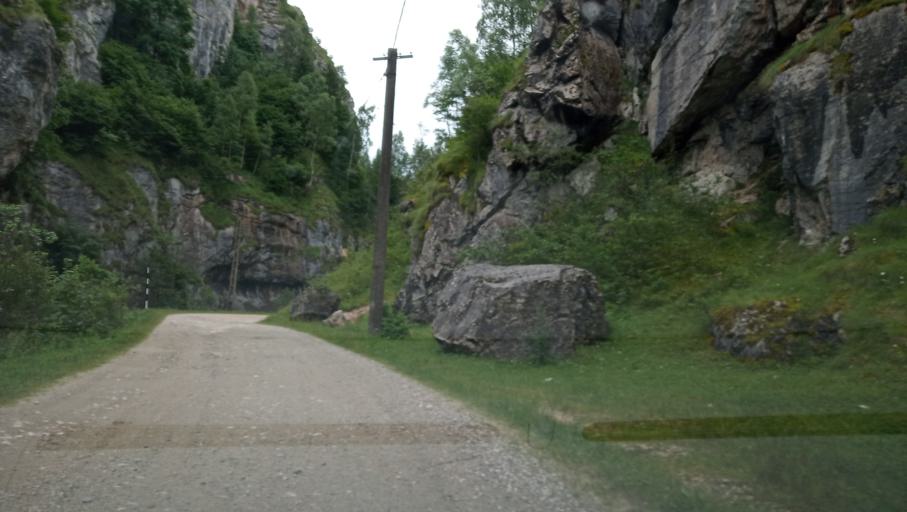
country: RO
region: Hunedoara
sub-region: Oras Petrila
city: Petrila
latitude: 45.4740
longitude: 23.4167
